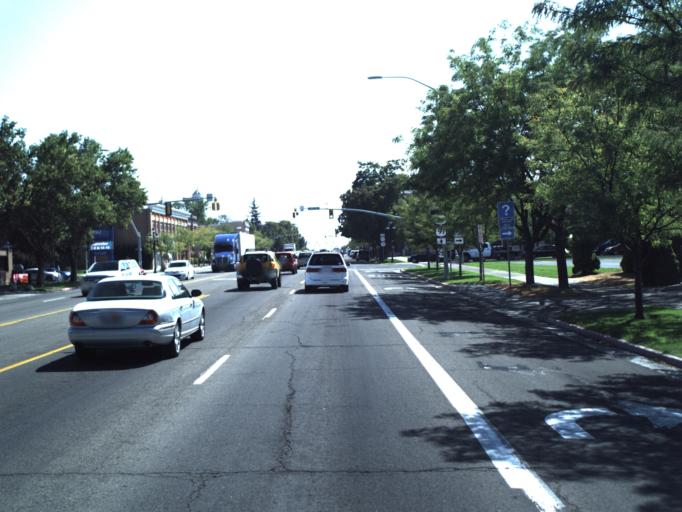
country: US
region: Utah
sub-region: Cache County
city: Logan
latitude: 41.7361
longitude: -111.8350
